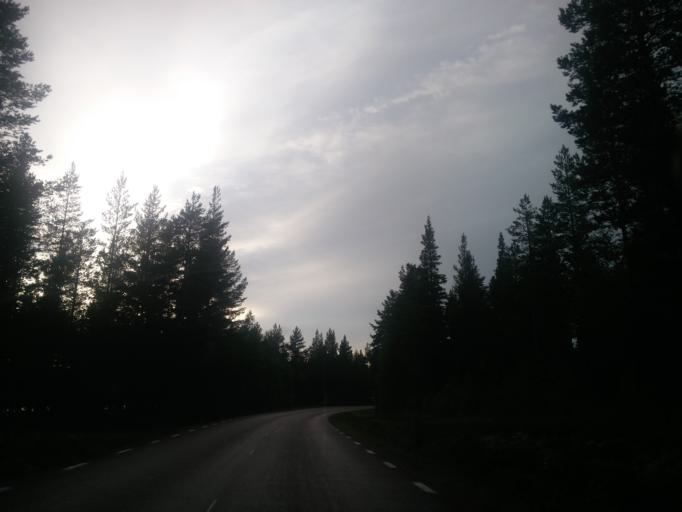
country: NO
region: Hedmark
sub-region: Trysil
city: Innbygda
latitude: 61.7857
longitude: 12.9327
